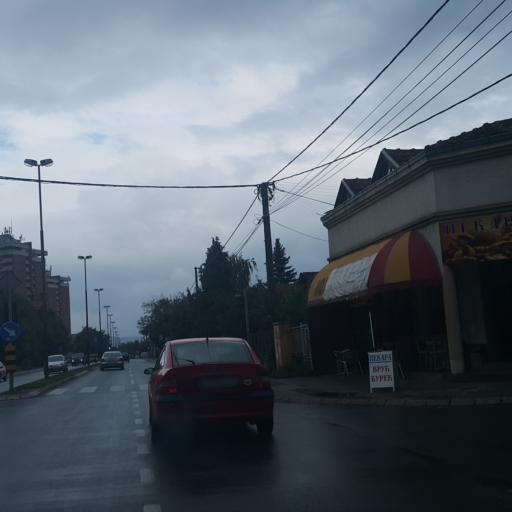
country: RS
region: Central Serbia
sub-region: Rasinski Okrug
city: Krusevac
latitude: 43.5728
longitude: 21.3411
